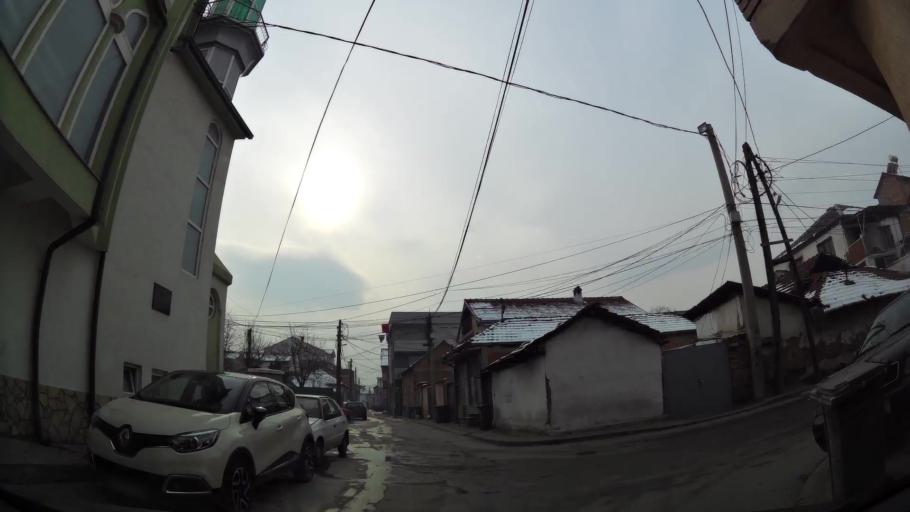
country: MK
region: Cair
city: Cair
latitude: 42.0054
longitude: 21.4444
